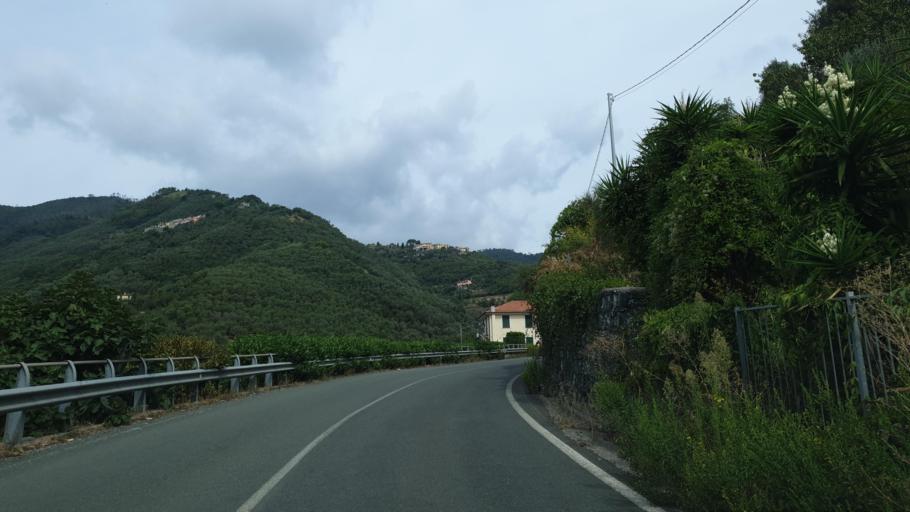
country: IT
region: Liguria
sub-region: Provincia di La Spezia
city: Levanto
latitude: 44.1844
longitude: 9.6208
